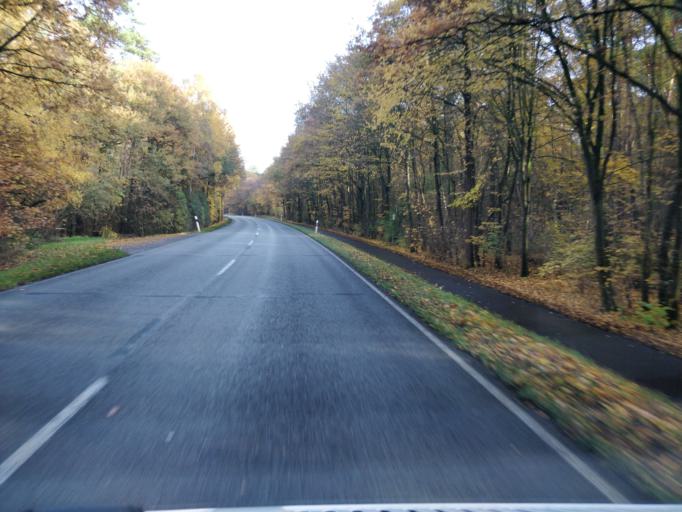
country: DE
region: North Rhine-Westphalia
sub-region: Regierungsbezirk Dusseldorf
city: Mehrhoog
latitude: 51.7184
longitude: 6.5179
